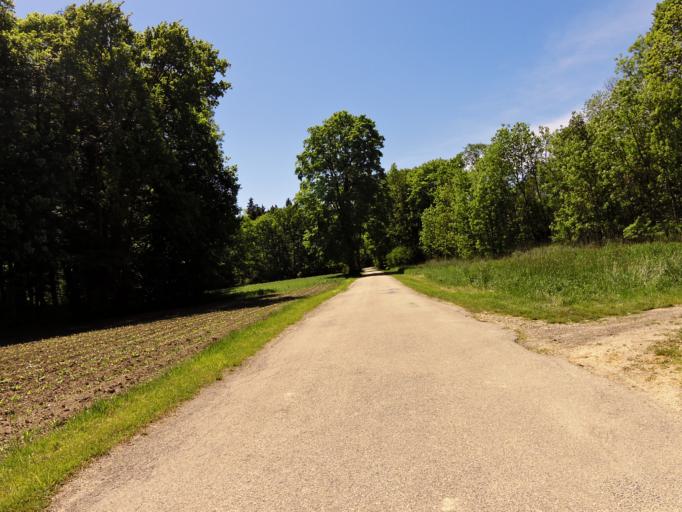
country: DE
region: Bavaria
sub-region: Upper Bavaria
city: Langenbach
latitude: 48.4572
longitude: 11.8636
